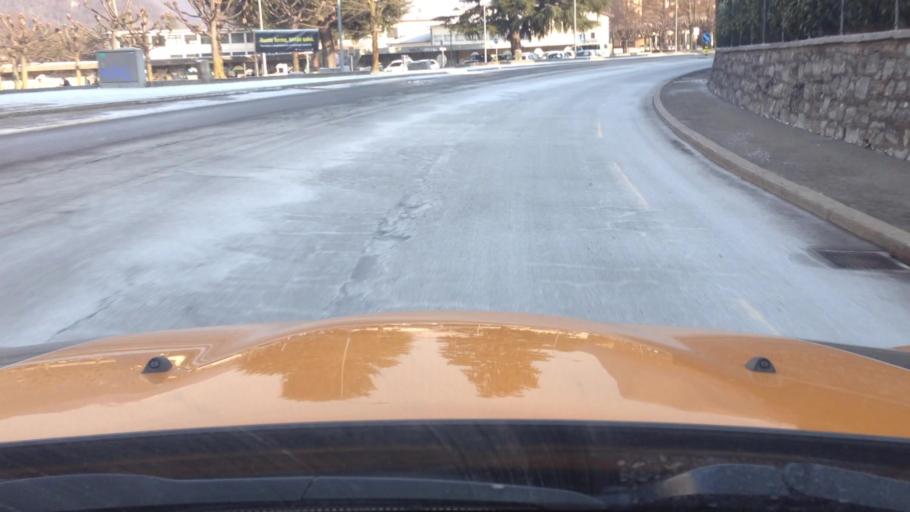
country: CH
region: Ticino
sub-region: Mendrisio District
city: Mendrisio
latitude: 45.8614
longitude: 8.9806
